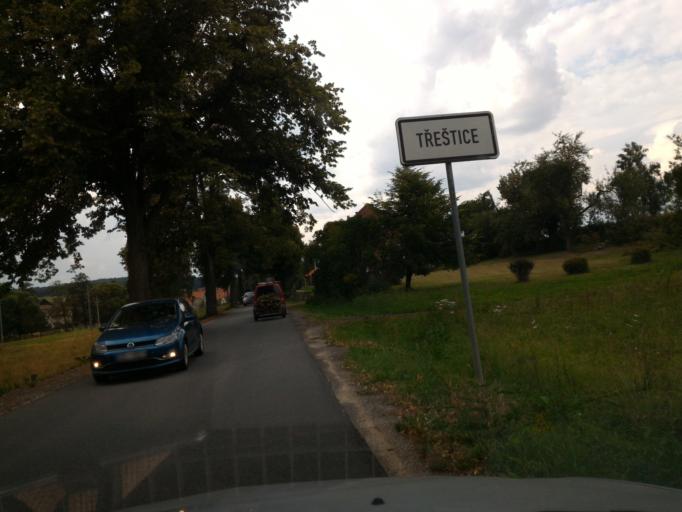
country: CZ
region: Vysocina
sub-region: Okres Jihlava
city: Trest'
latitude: 49.2434
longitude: 15.4570
